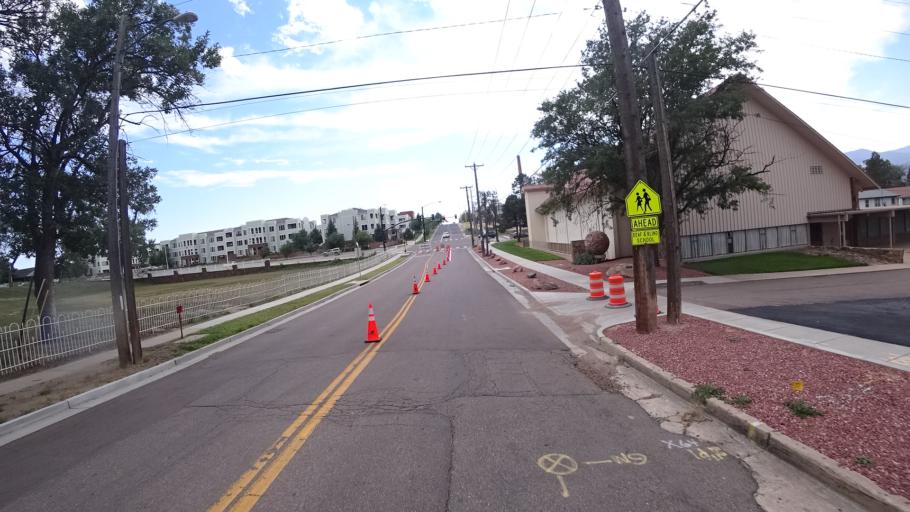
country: US
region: Colorado
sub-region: El Paso County
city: Colorado Springs
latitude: 38.8342
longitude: -104.8081
